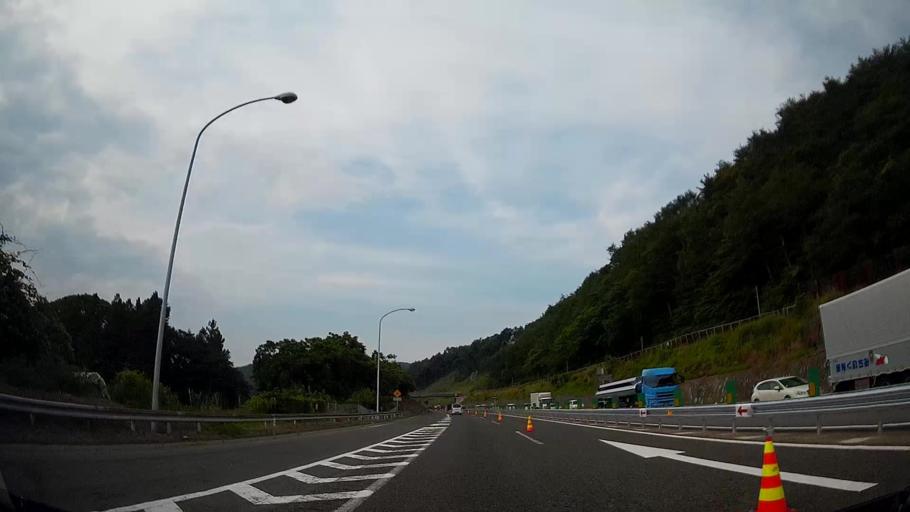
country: JP
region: Nagano
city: Tatsuno
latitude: 35.9774
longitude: 138.0048
